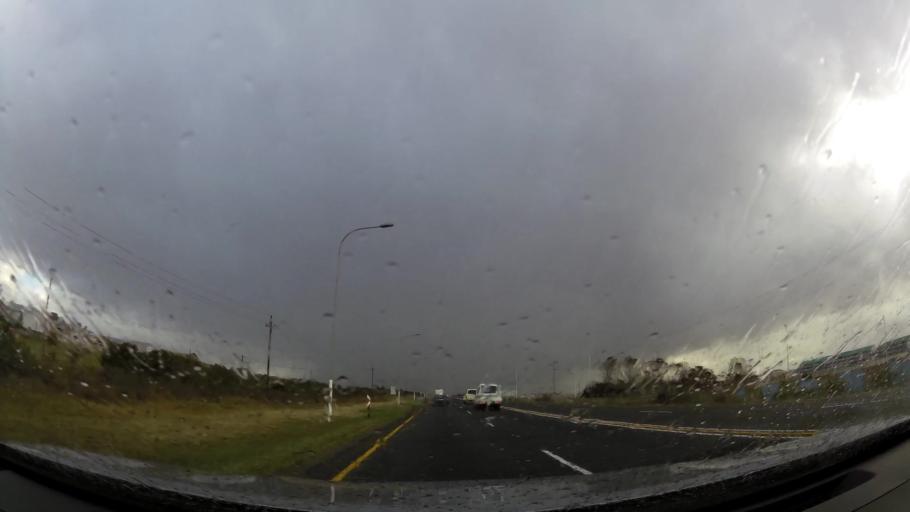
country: ZA
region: Western Cape
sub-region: Eden District Municipality
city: Mossel Bay
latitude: -34.1830
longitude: 22.0988
